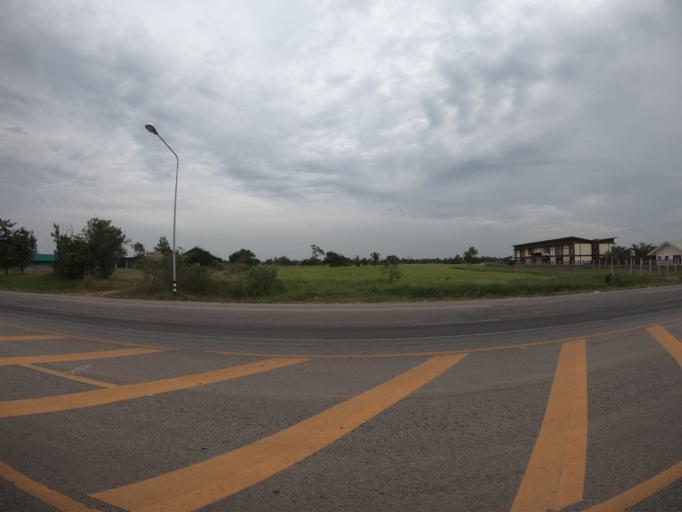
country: TH
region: Roi Et
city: Chiang Khwan
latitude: 16.1356
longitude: 103.8541
